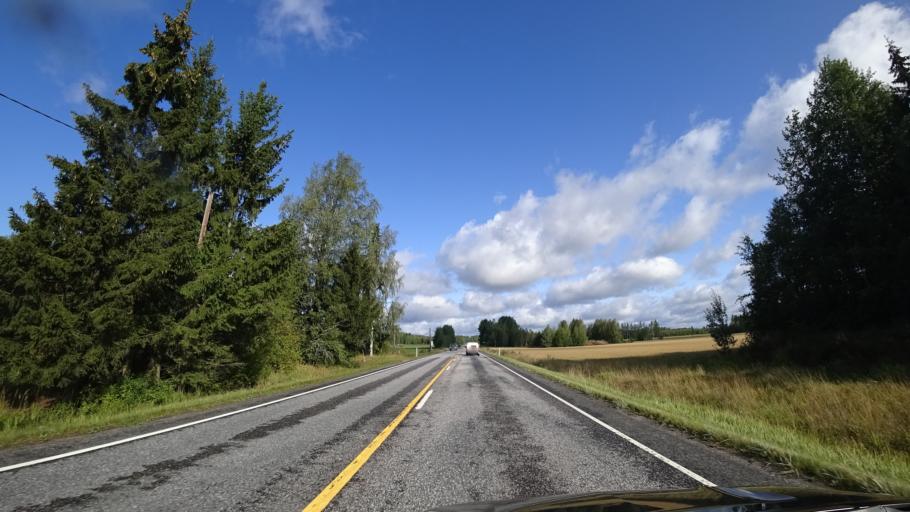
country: FI
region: Uusimaa
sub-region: Helsinki
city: Tuusula
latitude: 60.4634
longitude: 24.9466
